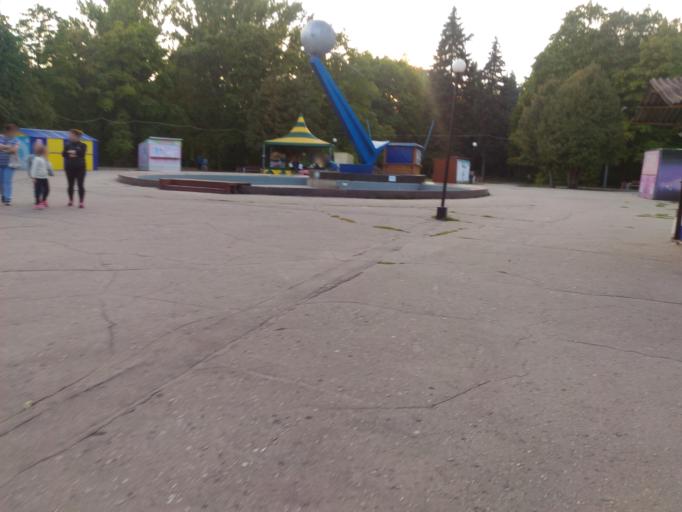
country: RU
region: Ulyanovsk
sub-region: Ulyanovskiy Rayon
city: Ulyanovsk
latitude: 54.3033
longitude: 48.3258
